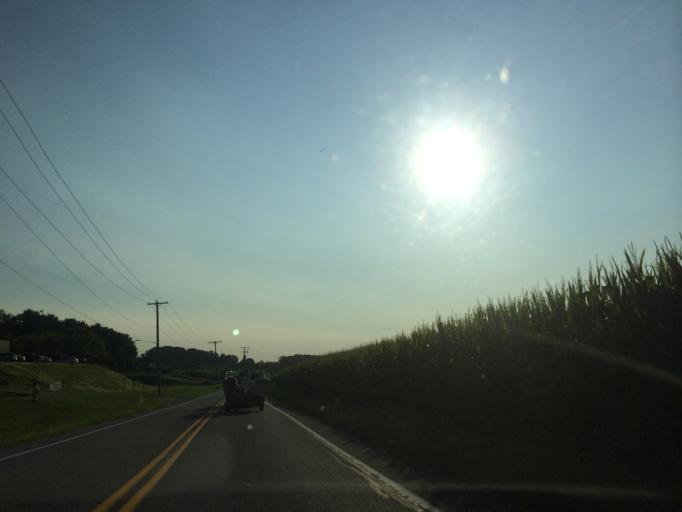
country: US
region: Pennsylvania
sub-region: York County
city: Loganville
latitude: 39.8263
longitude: -76.6912
